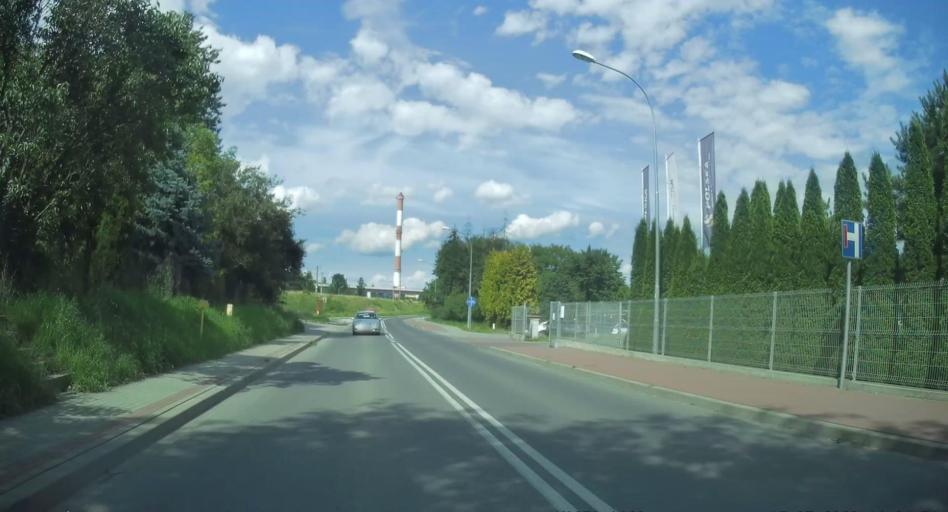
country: PL
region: Subcarpathian Voivodeship
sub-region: Przemysl
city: Przemysl
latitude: 49.7954
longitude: 22.7794
